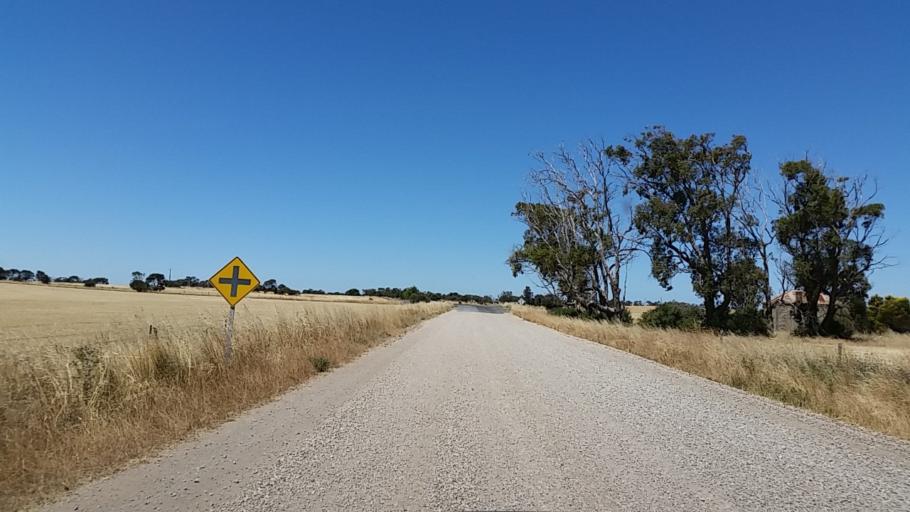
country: AU
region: South Australia
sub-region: Yorke Peninsula
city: Honiton
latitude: -35.0700
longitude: 137.5313
